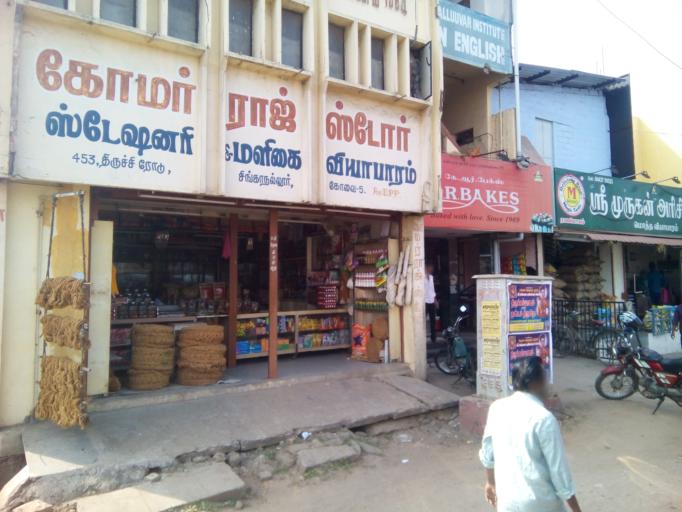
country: IN
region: Tamil Nadu
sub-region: Coimbatore
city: Singanallur
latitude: 11.0013
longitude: 77.0342
